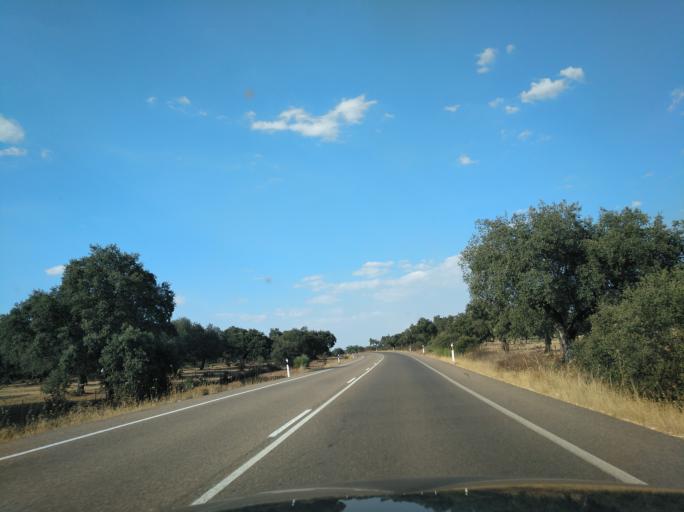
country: ES
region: Extremadura
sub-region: Provincia de Badajoz
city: Villanueva del Fresno
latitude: 38.3862
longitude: -7.1517
